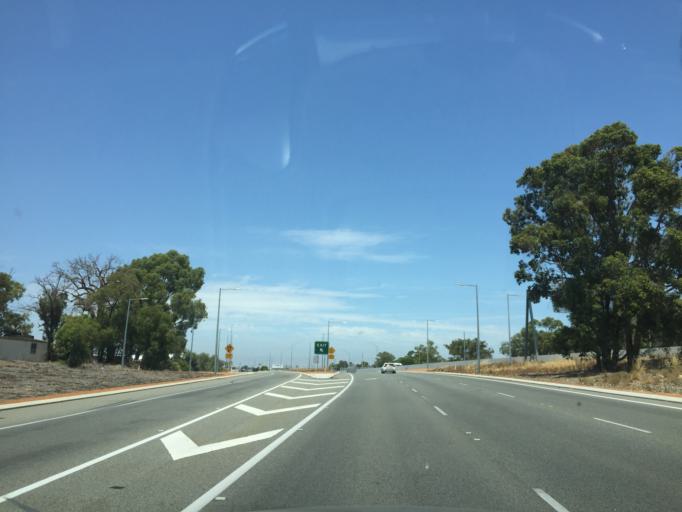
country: AU
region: Western Australia
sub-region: Belmont
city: Kewdale
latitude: -31.9689
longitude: 115.9532
